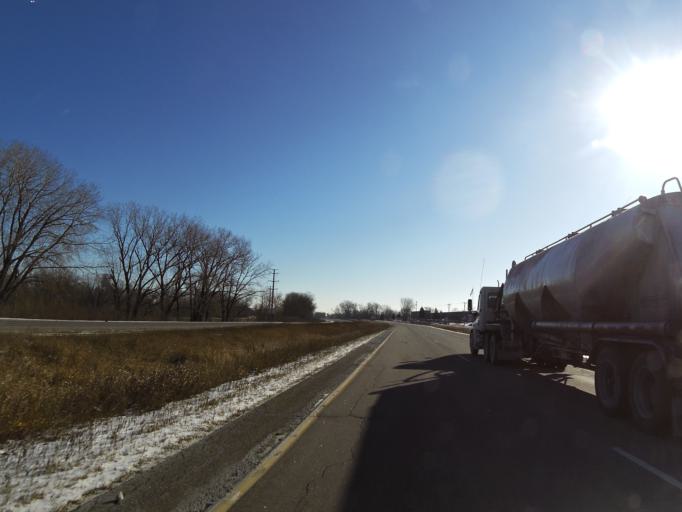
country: US
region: Minnesota
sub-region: Scott County
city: Savage
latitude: 44.7779
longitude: -93.3674
